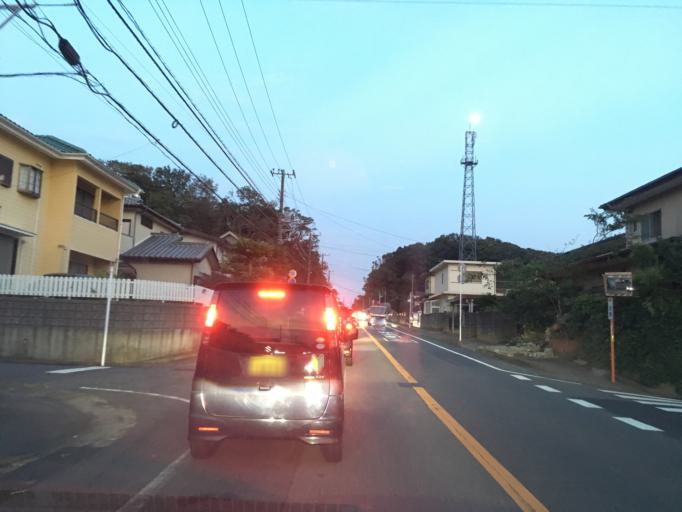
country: JP
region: Chiba
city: Kisarazu
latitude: 35.3462
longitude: 139.9158
